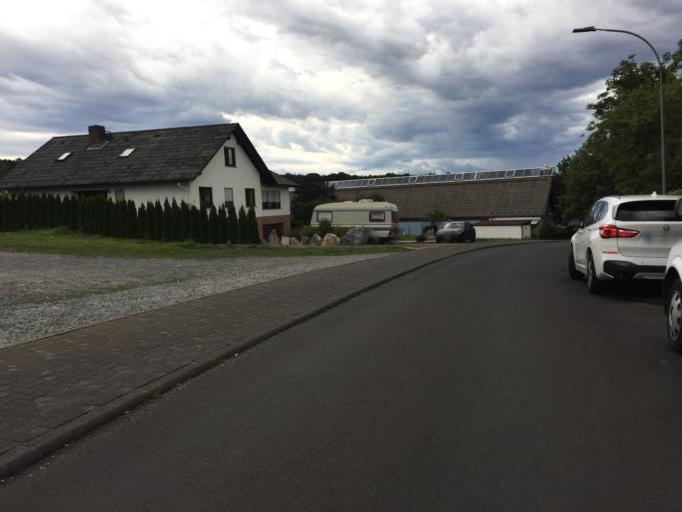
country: DE
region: Hesse
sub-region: Regierungsbezirk Giessen
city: Langgons
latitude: 50.4900
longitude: 8.6753
